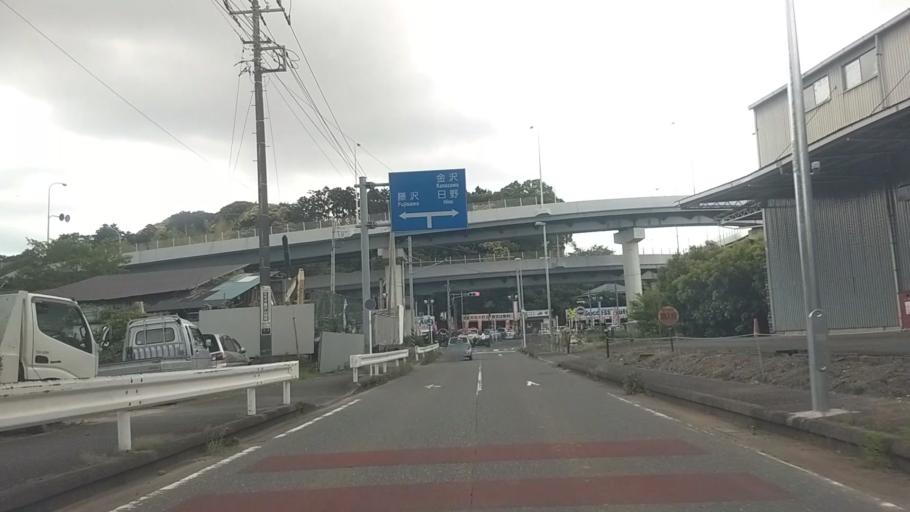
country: JP
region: Kanagawa
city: Fujisawa
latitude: 35.3584
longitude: 139.5099
